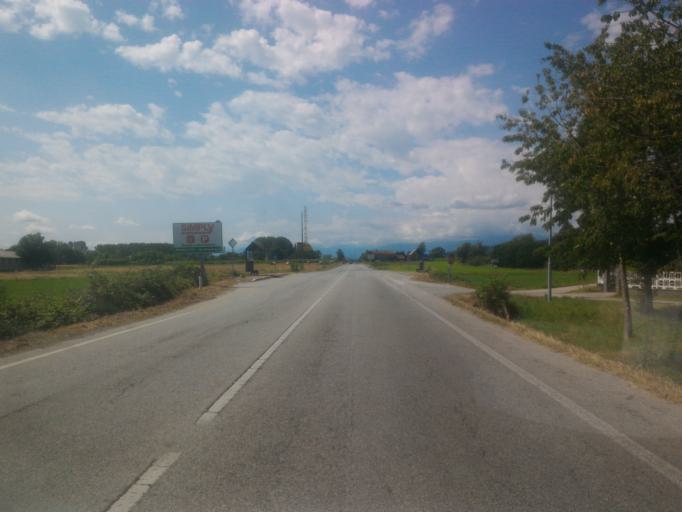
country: IT
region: Piedmont
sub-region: Provincia di Torino
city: Frossasco
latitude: 44.9359
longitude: 7.3718
